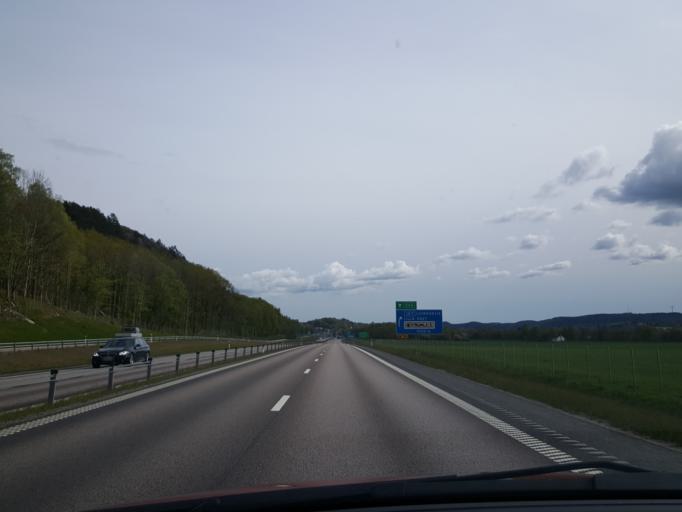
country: SE
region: Vaestra Goetaland
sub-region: Lilla Edets Kommun
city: Lilla Edet
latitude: 58.1600
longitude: 12.1361
